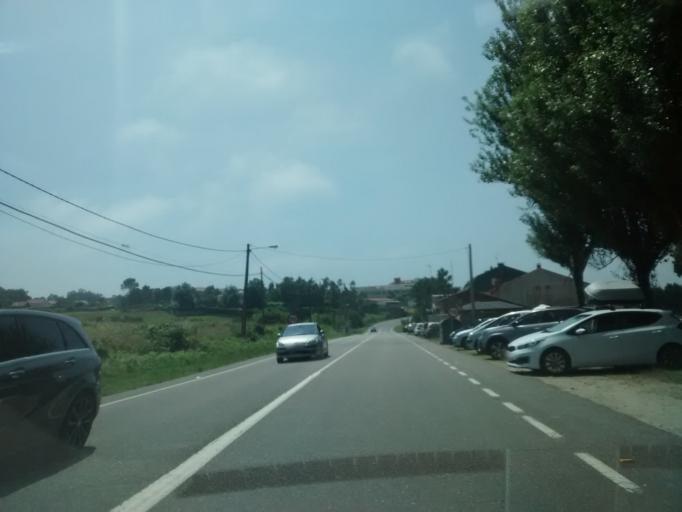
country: ES
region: Galicia
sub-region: Provincia de Pontevedra
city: Sanxenxo
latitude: 42.3965
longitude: -8.8446
